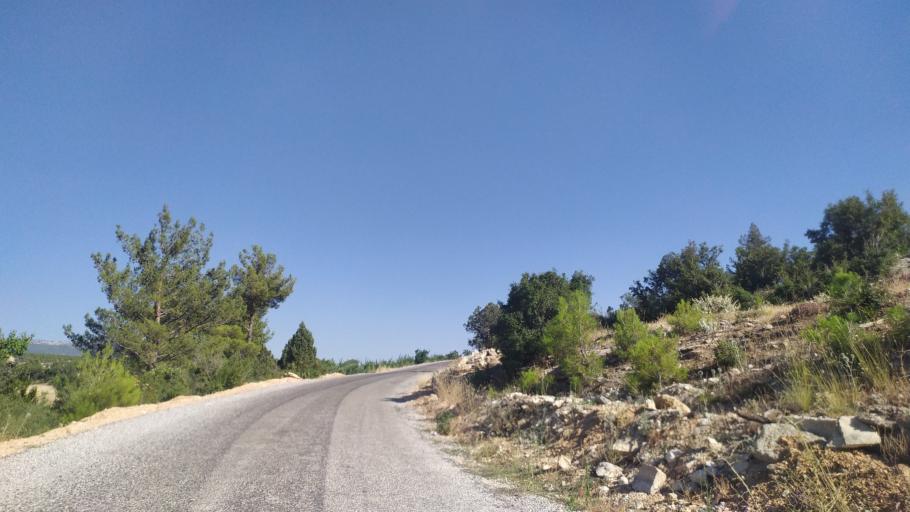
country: TR
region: Mersin
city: Mut
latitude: 36.7002
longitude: 33.4794
